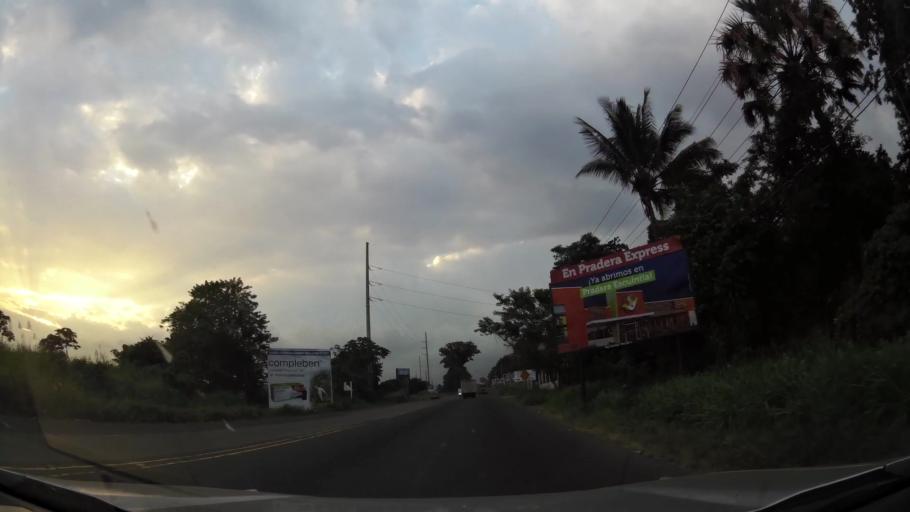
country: GT
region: Escuintla
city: Siquinala
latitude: 14.2955
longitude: -90.9463
